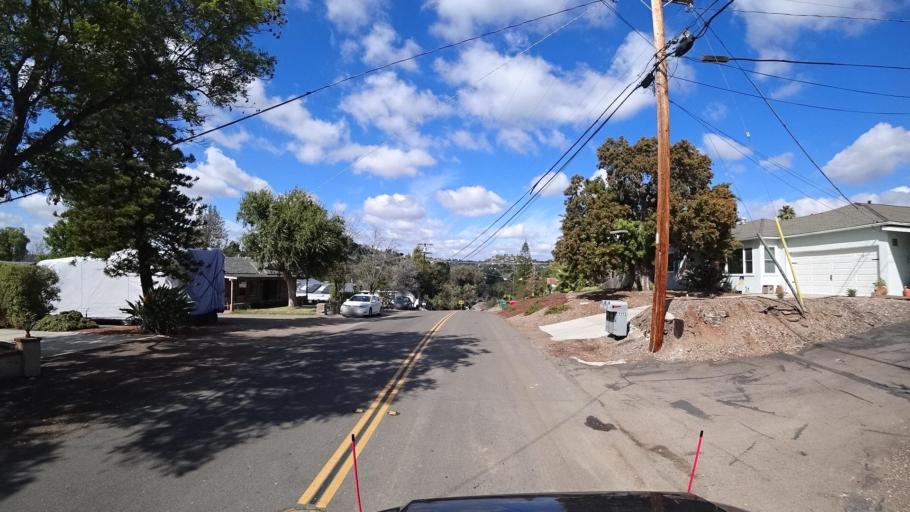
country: US
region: California
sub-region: San Diego County
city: Casa de Oro-Mount Helix
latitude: 32.7433
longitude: -116.9634
